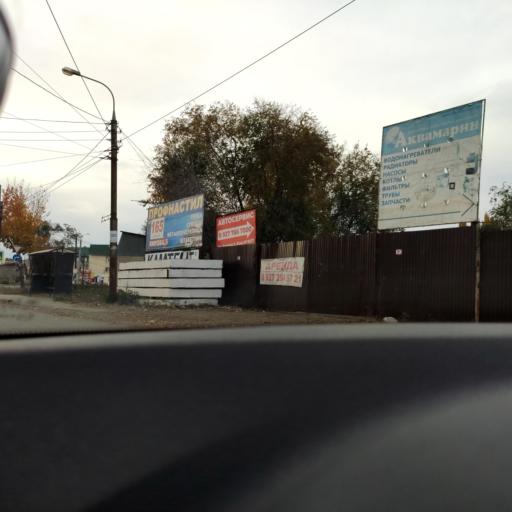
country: RU
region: Samara
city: Smyshlyayevka
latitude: 53.1931
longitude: 50.2945
